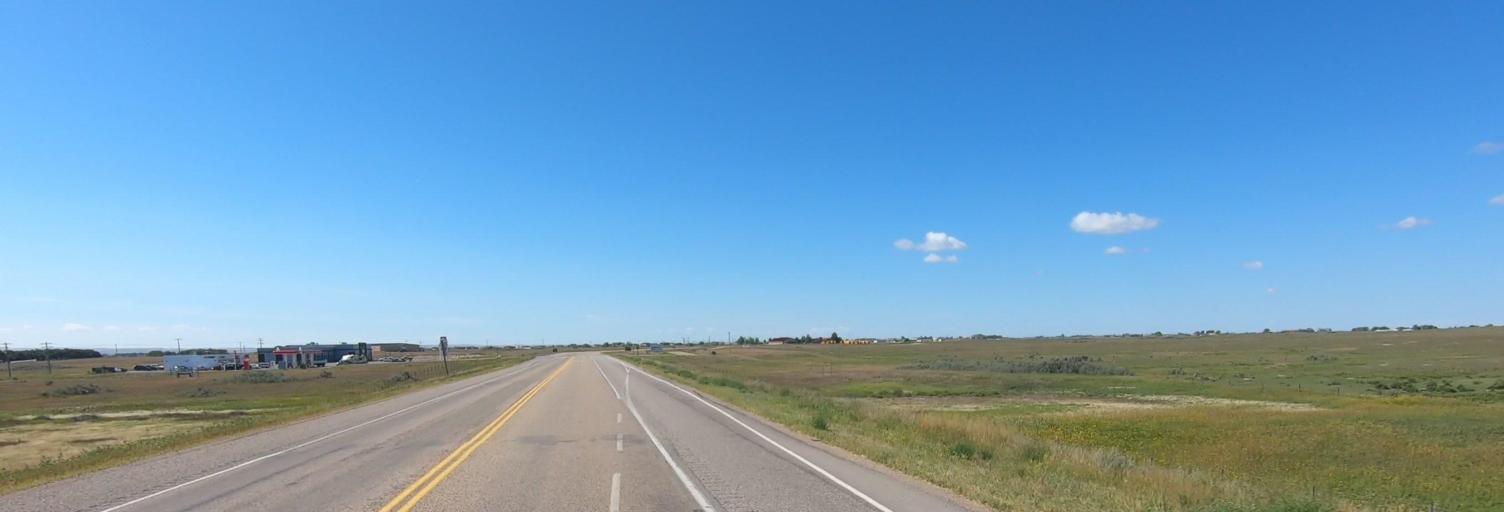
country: CA
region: Alberta
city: Strathmore
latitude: 50.8544
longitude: -113.0179
